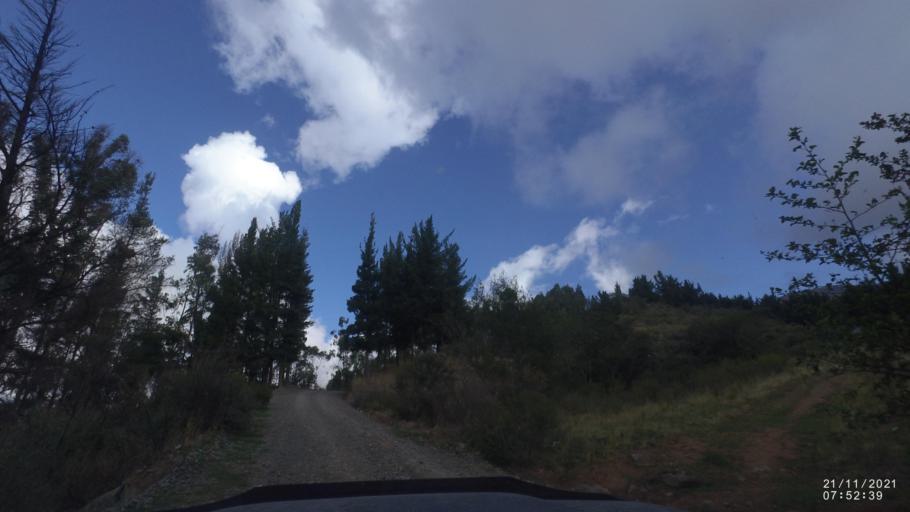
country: BO
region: Cochabamba
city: Cochabamba
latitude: -17.3046
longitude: -66.2181
